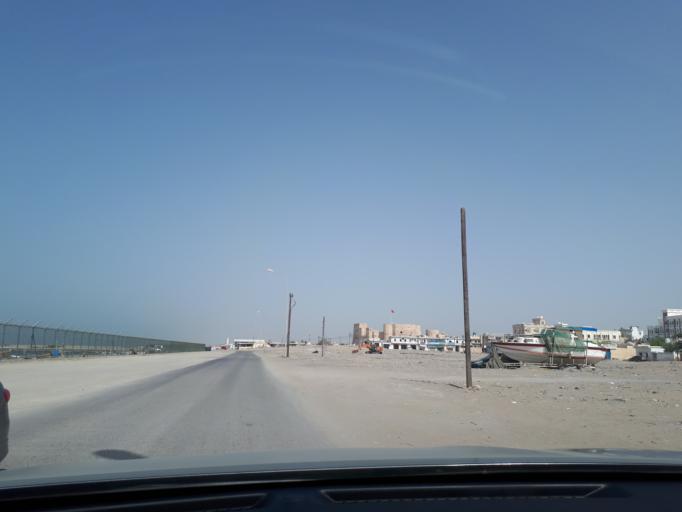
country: OM
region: Al Batinah
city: Barka'
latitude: 23.7099
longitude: 57.8918
